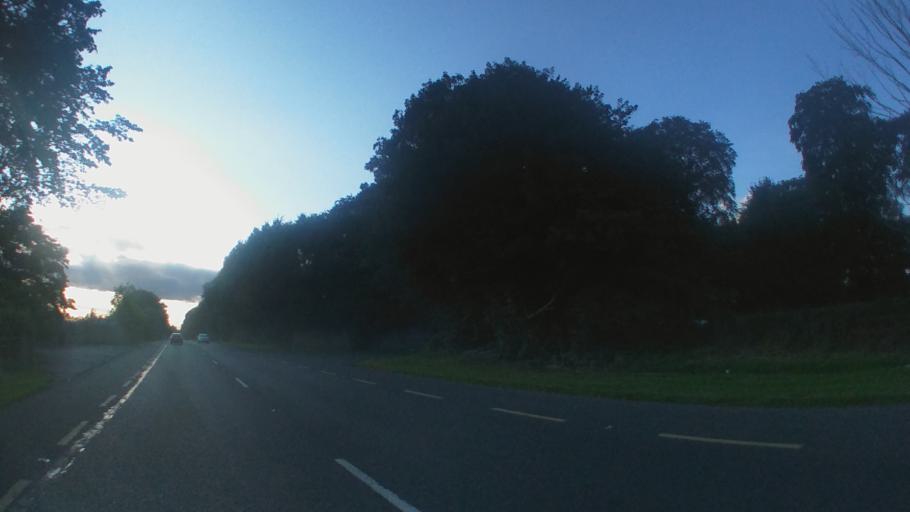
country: IE
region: Leinster
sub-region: Lu
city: Dundalk
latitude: 54.0334
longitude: -6.3638
